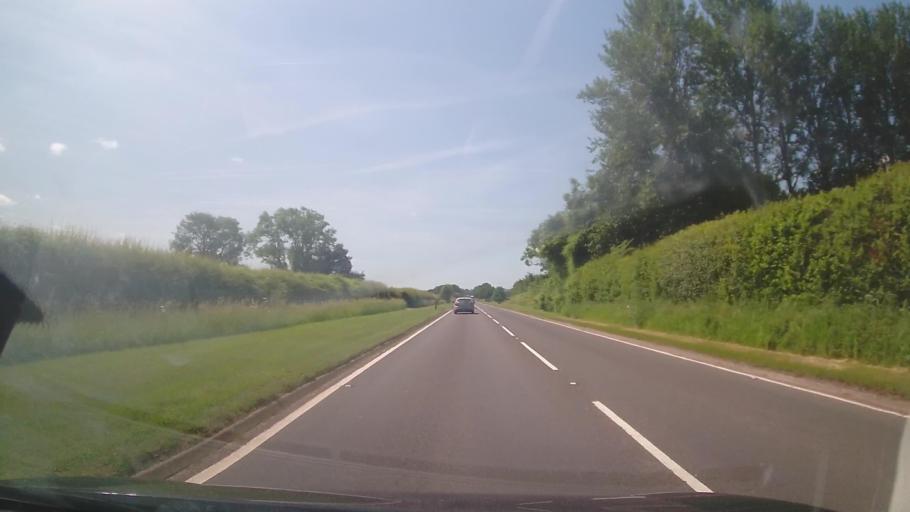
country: GB
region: England
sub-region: Herefordshire
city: Dinmore
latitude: 52.1441
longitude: -2.7279
